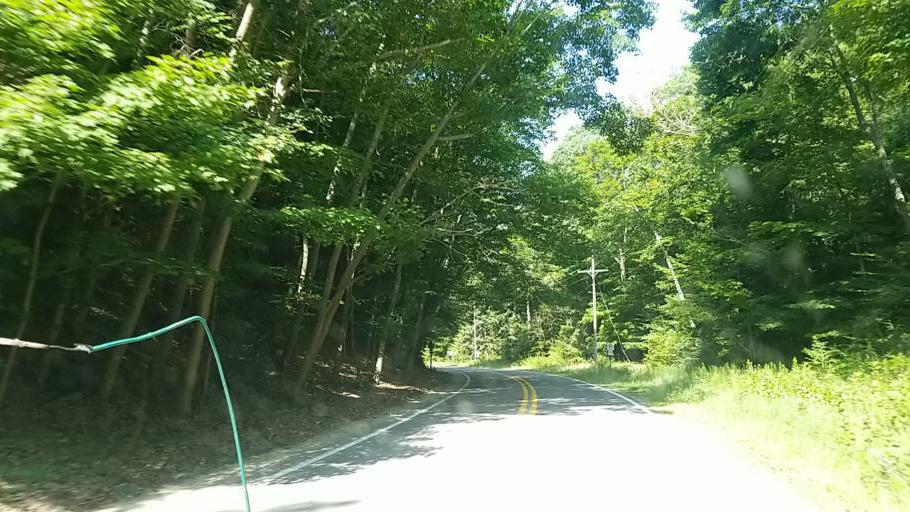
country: US
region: Michigan
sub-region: Muskegon County
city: Whitehall
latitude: 43.3393
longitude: -86.4033
